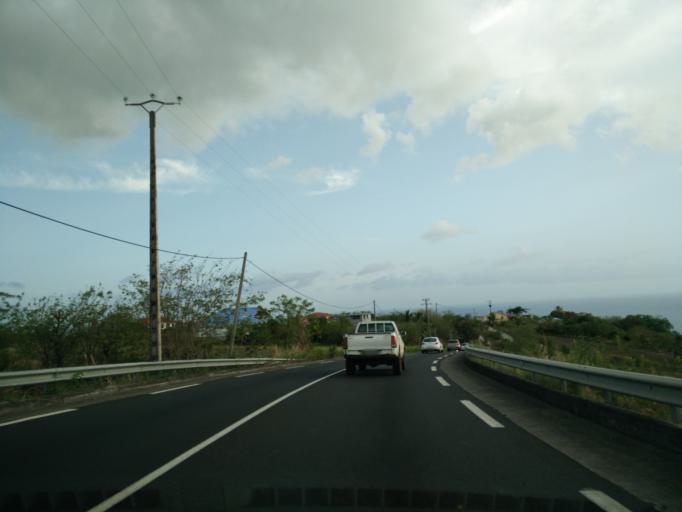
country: MQ
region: Martinique
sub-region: Martinique
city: Saint-Pierre
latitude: 14.6902
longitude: -61.1654
